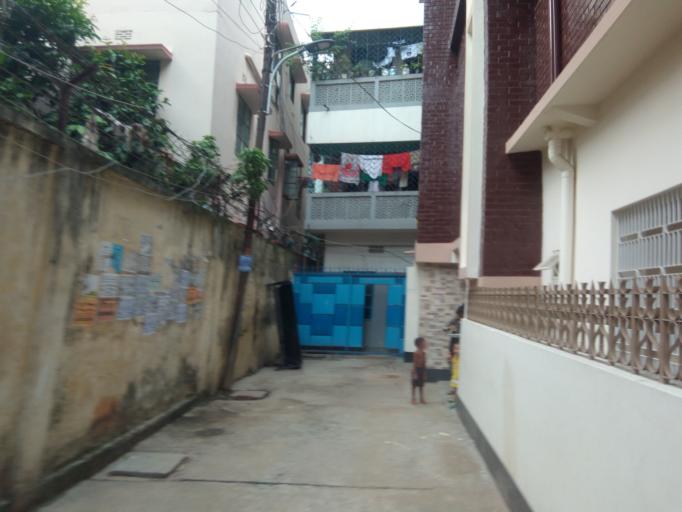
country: BD
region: Dhaka
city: Paltan
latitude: 23.7395
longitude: 90.4084
